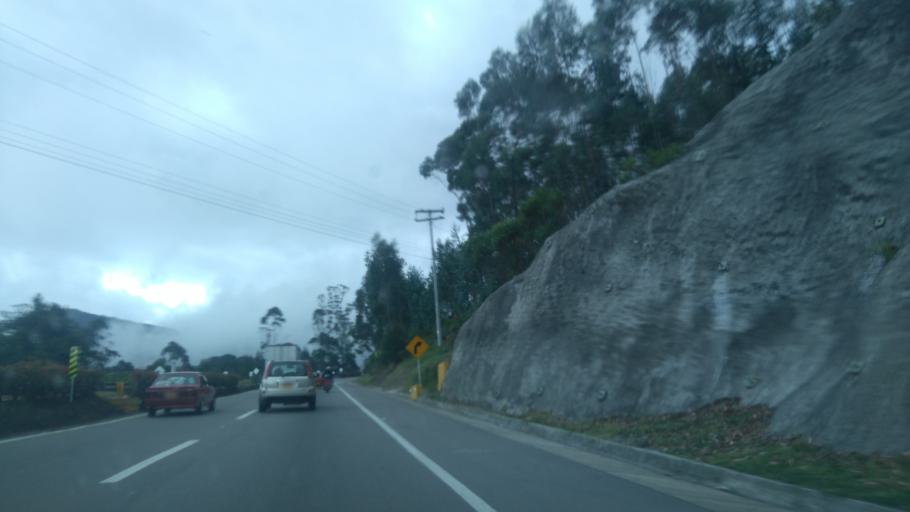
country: CO
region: Cundinamarca
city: El Rosal
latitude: 4.8906
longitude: -74.3042
